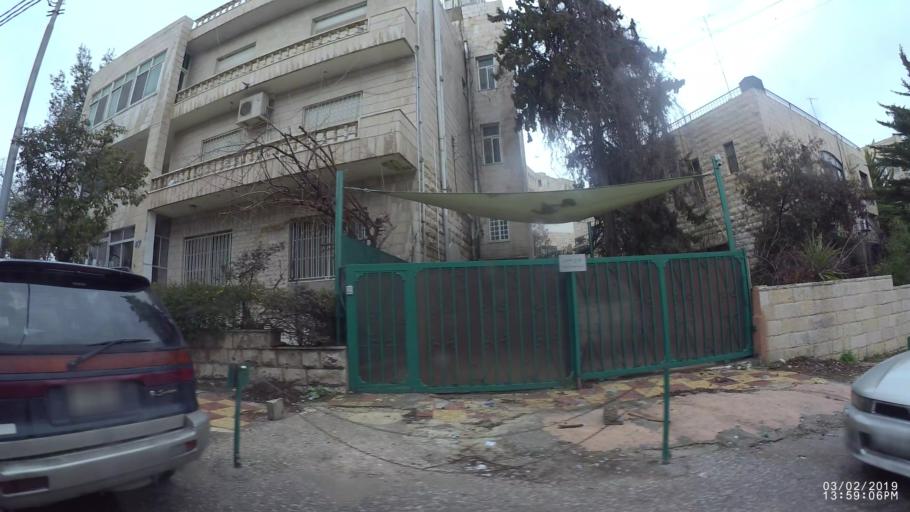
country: JO
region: Amman
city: Amman
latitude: 31.9622
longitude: 35.9000
